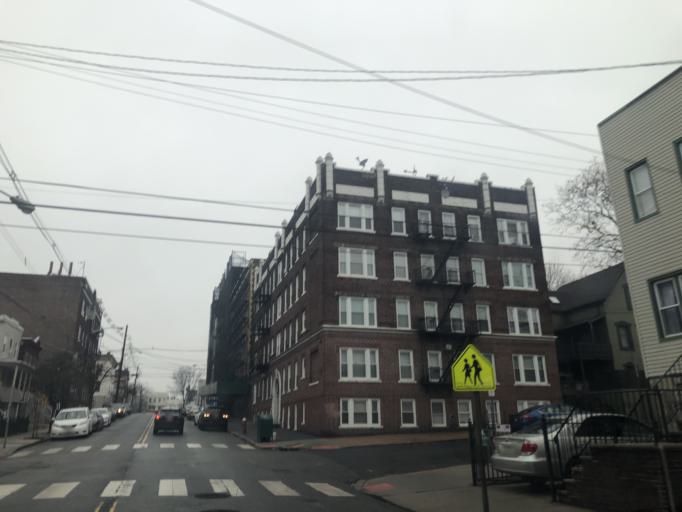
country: US
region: New Jersey
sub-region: Hudson County
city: Hoboken
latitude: 40.7498
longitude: -74.0433
